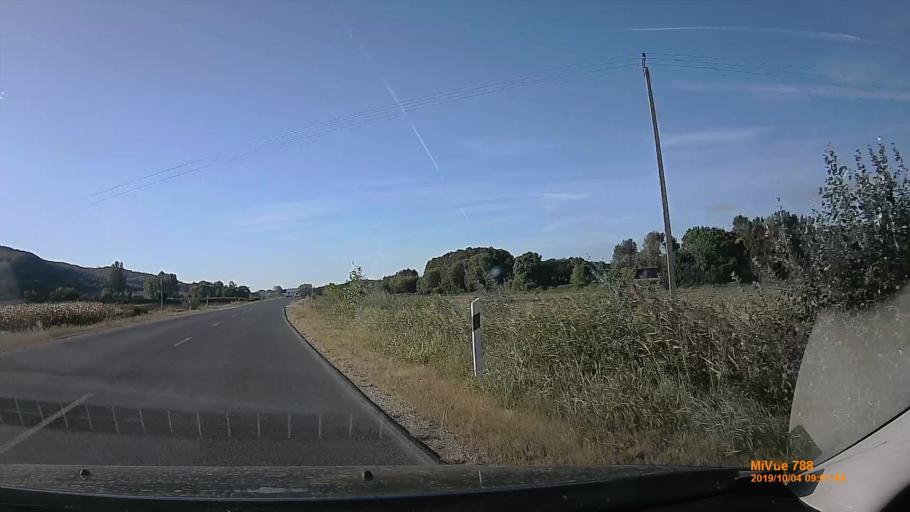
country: HU
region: Somogy
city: Karad
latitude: 46.7323
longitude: 17.7770
